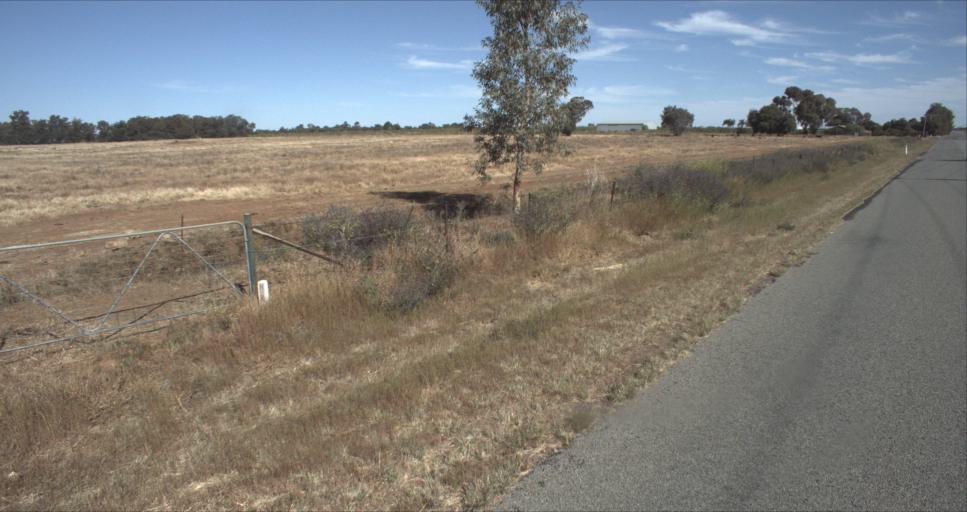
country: AU
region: New South Wales
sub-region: Leeton
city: Leeton
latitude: -34.5621
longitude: 146.3834
